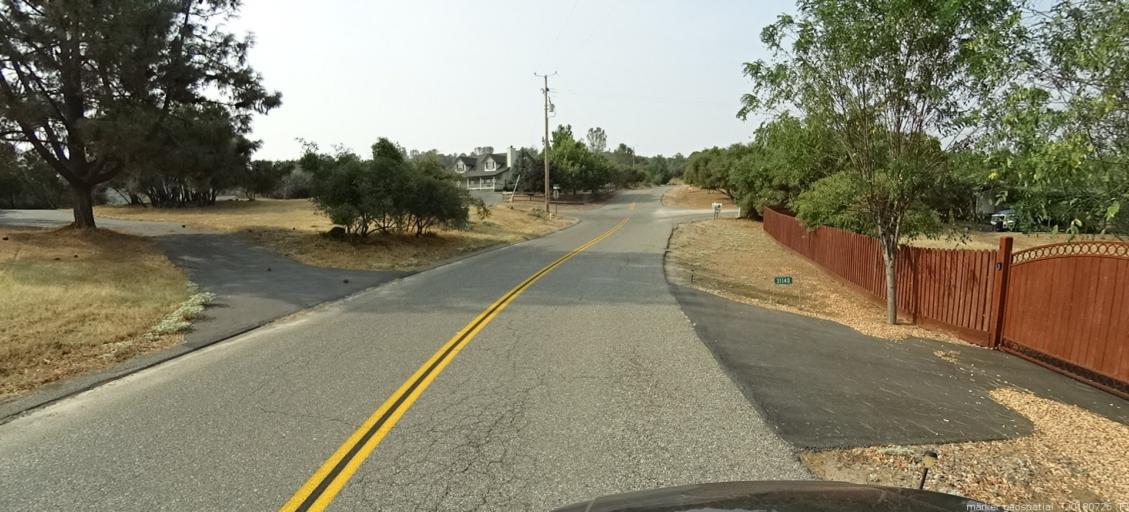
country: US
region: California
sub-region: Madera County
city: Coarsegold
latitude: 37.2015
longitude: -119.6879
